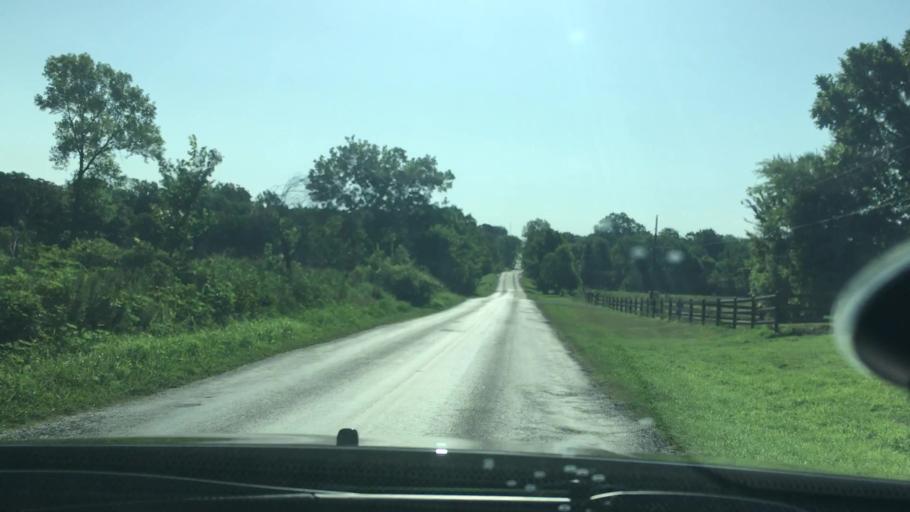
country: US
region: Oklahoma
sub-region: Pontotoc County
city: Ada
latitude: 34.8107
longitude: -96.6478
